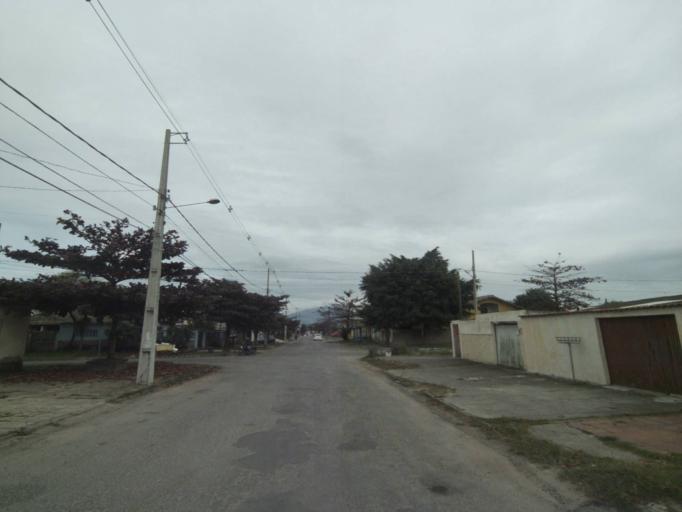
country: BR
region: Parana
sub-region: Paranagua
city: Paranagua
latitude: -25.5144
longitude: -48.5293
